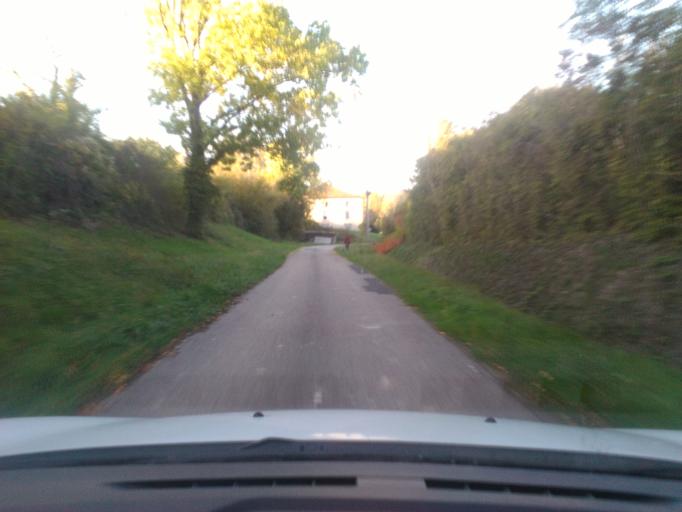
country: FR
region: Lorraine
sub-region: Departement des Vosges
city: Charmes
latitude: 48.3460
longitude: 6.2532
